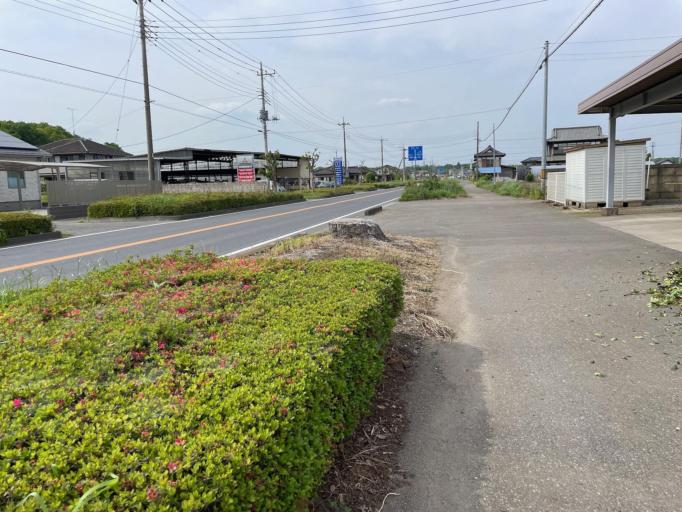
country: JP
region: Tochigi
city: Mibu
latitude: 36.3885
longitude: 139.8038
